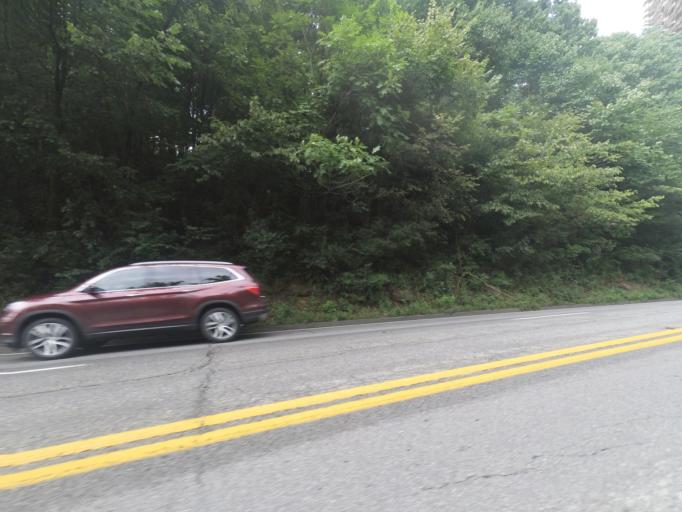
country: US
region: West Virginia
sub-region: Cabell County
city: Huntington
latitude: 38.3985
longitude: -82.4487
